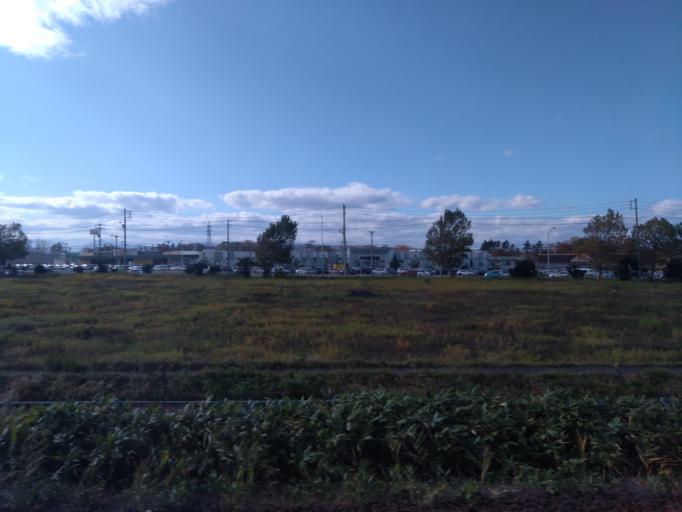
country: JP
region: Hokkaido
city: Kitahiroshima
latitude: 42.9055
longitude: 141.5743
